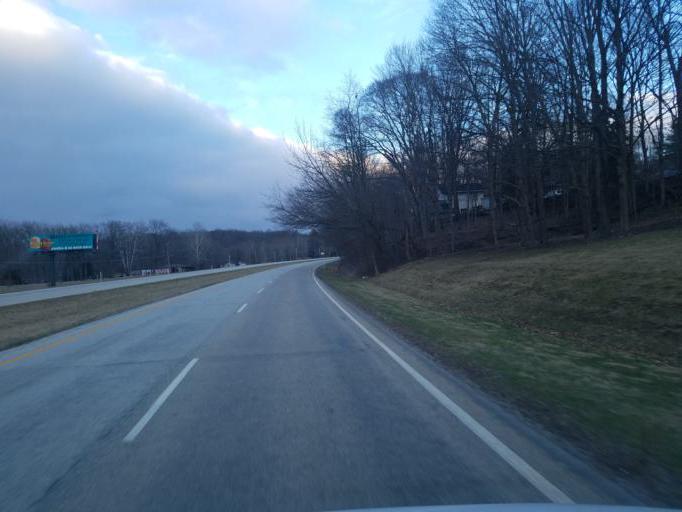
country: US
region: Indiana
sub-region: Henry County
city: Knightstown
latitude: 39.8032
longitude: -85.5022
